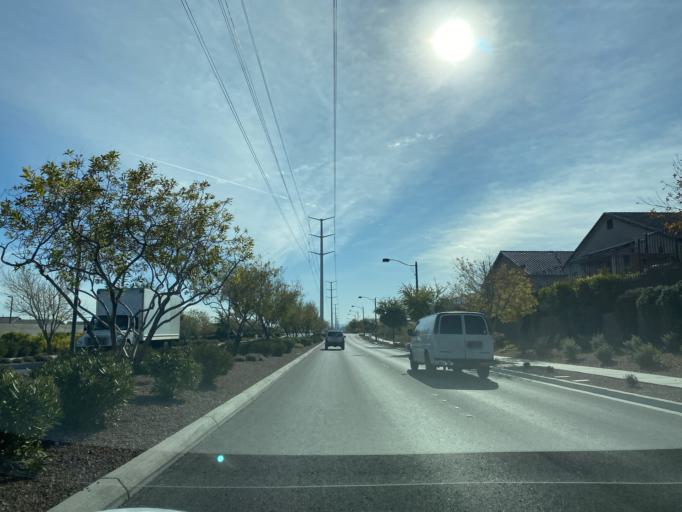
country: US
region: Nevada
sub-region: Clark County
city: Summerlin South
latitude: 36.2929
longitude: -115.3289
